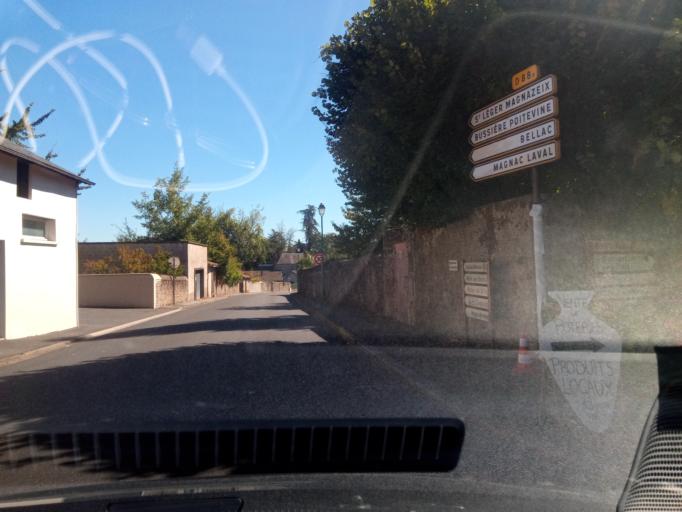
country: FR
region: Limousin
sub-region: Departement de la Haute-Vienne
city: Le Dorat
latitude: 46.2170
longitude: 1.0805
